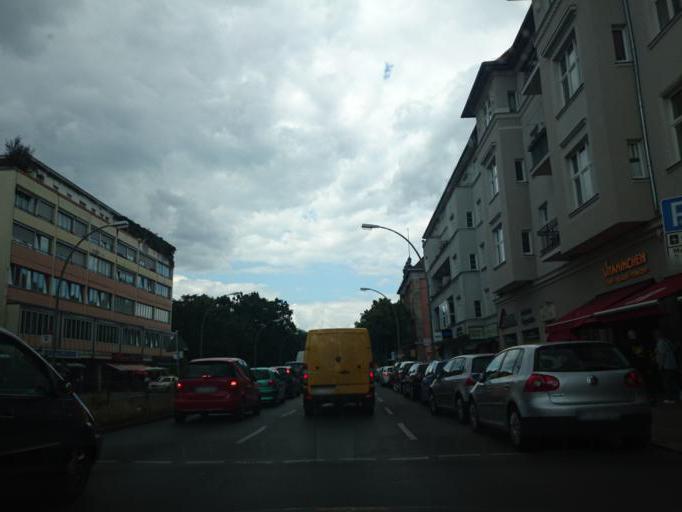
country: DE
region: Berlin
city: Tempelhof Bezirk
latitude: 52.4609
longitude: 13.3850
